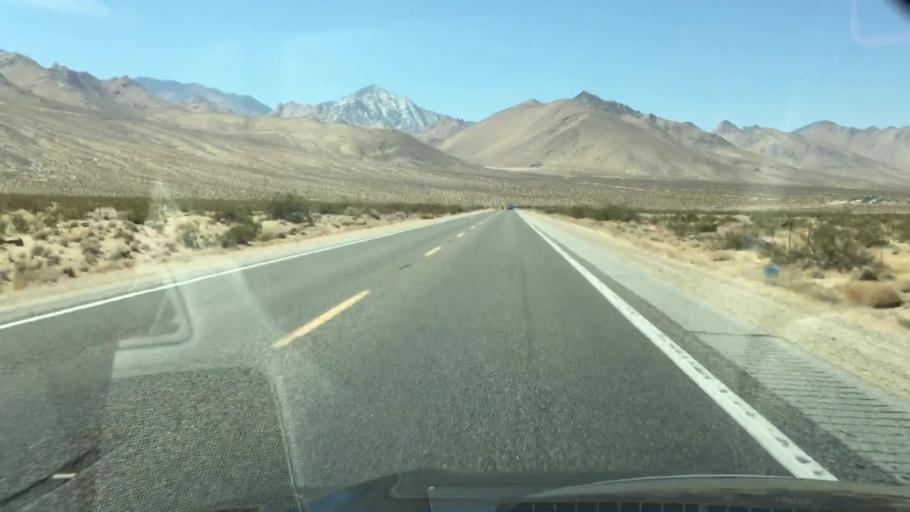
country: US
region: California
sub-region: Kern County
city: Inyokern
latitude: 35.6878
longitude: -117.8547
